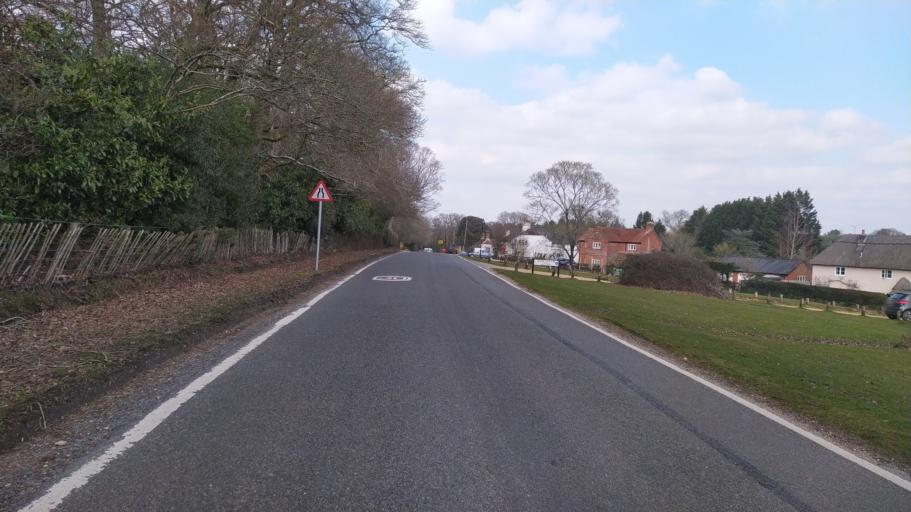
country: GB
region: England
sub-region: Hampshire
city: Cadnam
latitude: 50.9289
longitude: -1.6168
